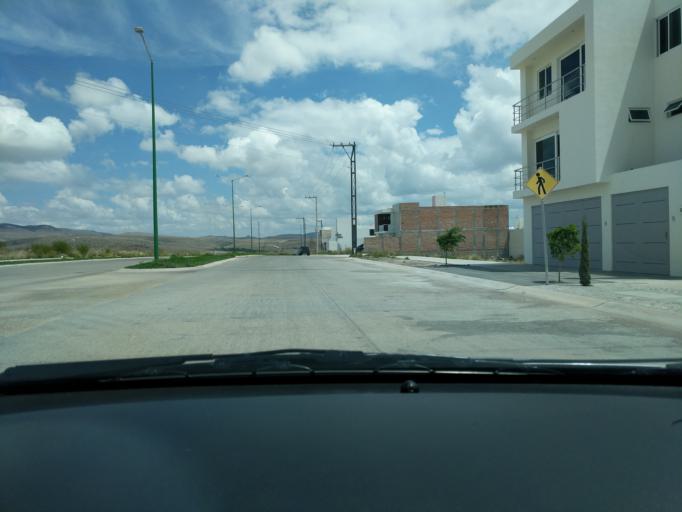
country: MX
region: San Luis Potosi
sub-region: Mexquitic de Carmona
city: Guadalupe Victoria
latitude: 22.1592
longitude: -101.0549
